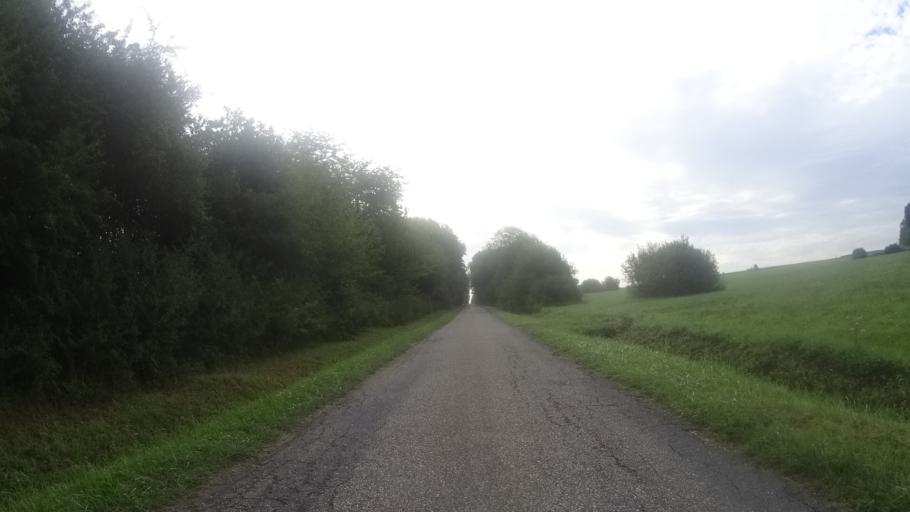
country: FR
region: Lorraine
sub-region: Departement de la Moselle
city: Niderviller
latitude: 48.7249
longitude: 7.1480
